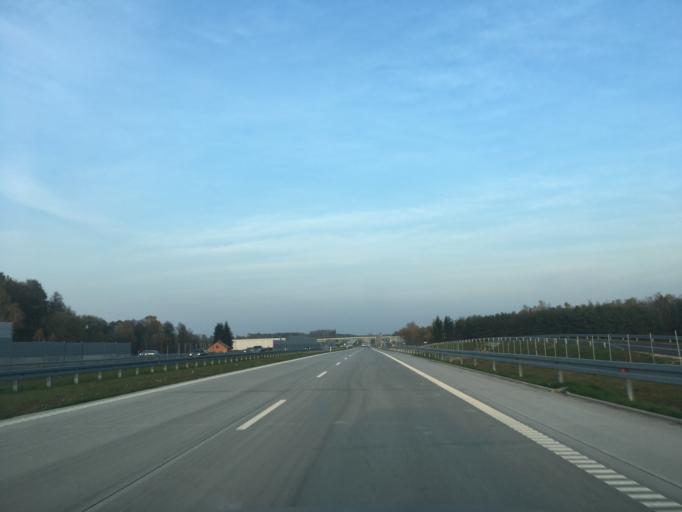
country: PL
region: Lodz Voivodeship
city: Zabia Wola
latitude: 52.0156
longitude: 20.6232
